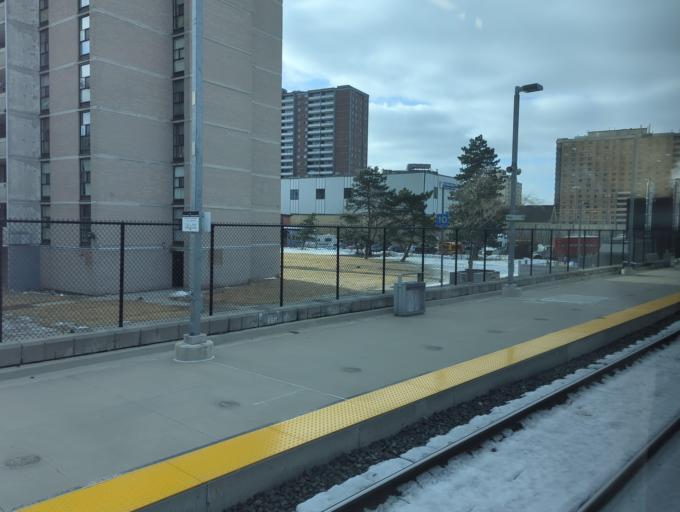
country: CA
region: Ontario
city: Etobicoke
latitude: 43.6997
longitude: -79.5123
